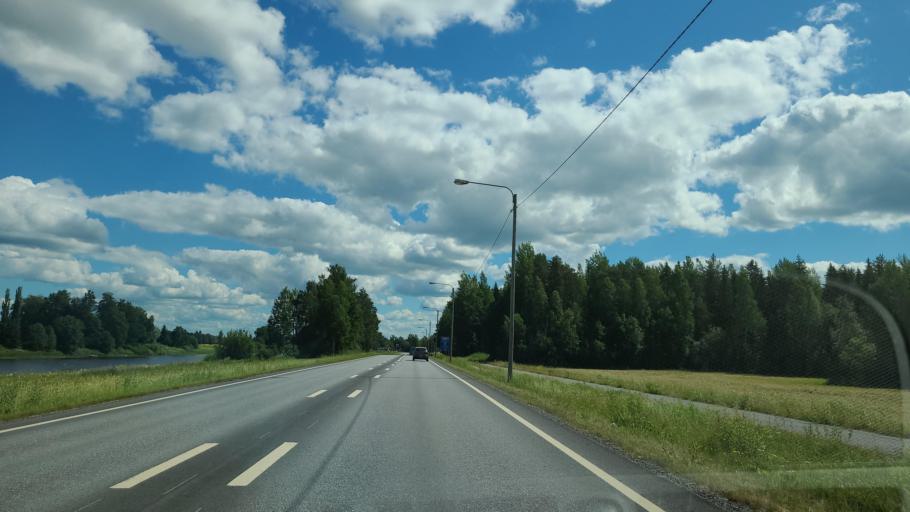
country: FI
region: Ostrobothnia
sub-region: Kyroenmaa
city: Isokyroe
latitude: 62.9744
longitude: 22.3711
